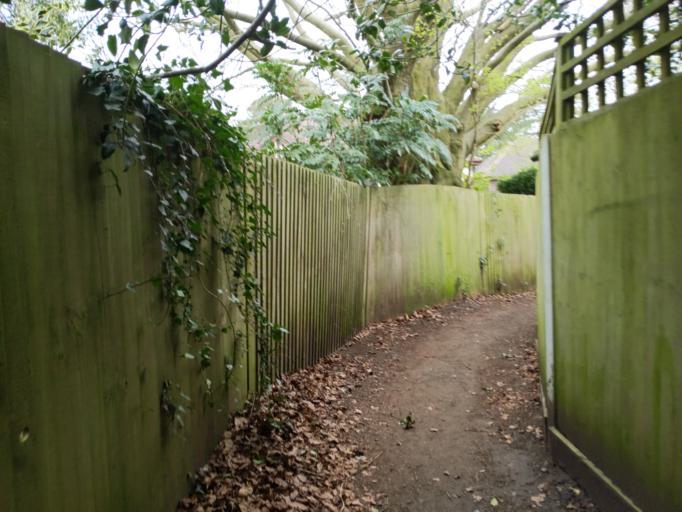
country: GB
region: England
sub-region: Surrey
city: Esher
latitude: 51.3640
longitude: -0.3520
